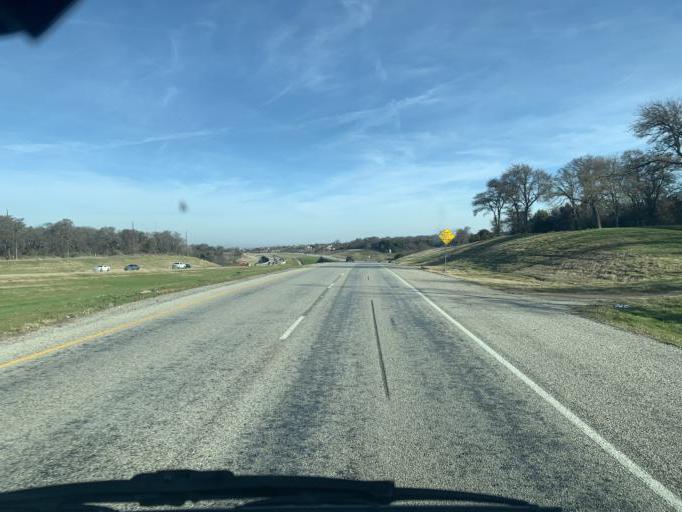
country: US
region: Texas
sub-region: Dallas County
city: Cedar Hill
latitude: 32.6331
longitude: -96.9734
